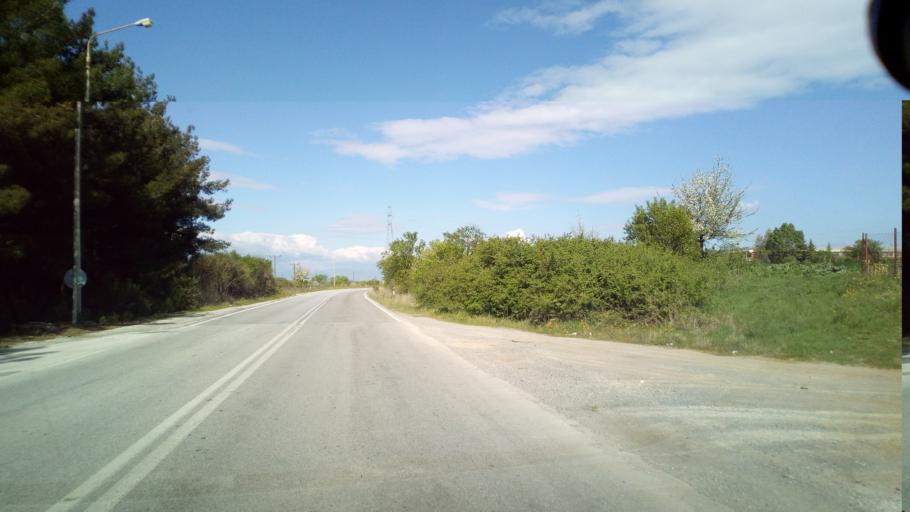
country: GR
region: Central Macedonia
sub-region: Nomos Kilkis
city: Nea Santa
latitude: 40.8346
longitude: 22.9122
